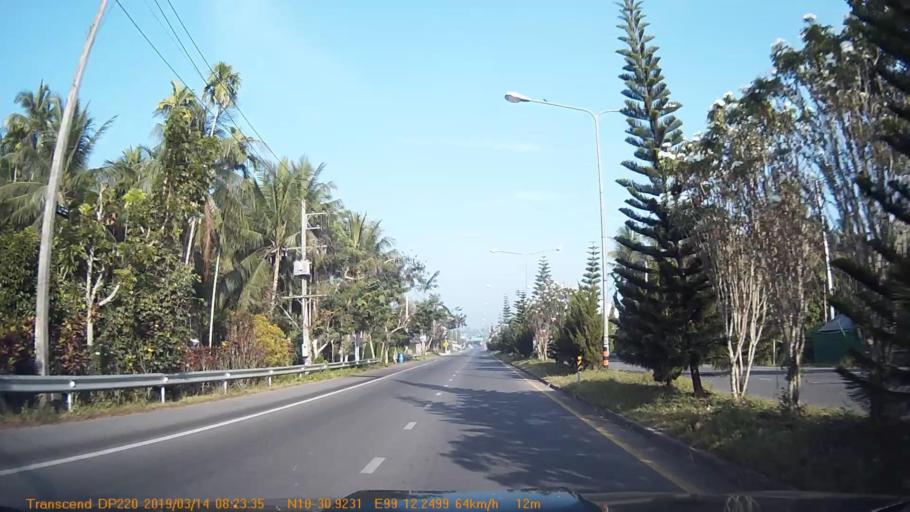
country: TH
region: Chumphon
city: Chumphon
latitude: 10.5155
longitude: 99.2040
